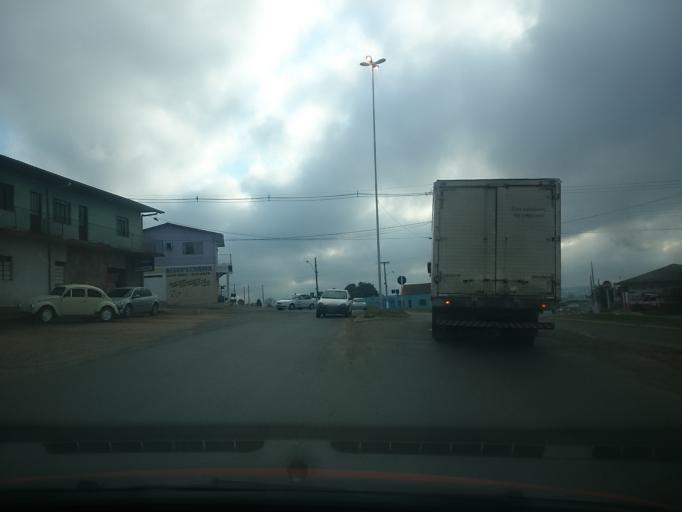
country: BR
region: Santa Catarina
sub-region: Lages
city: Lages
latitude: -27.8331
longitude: -50.3484
